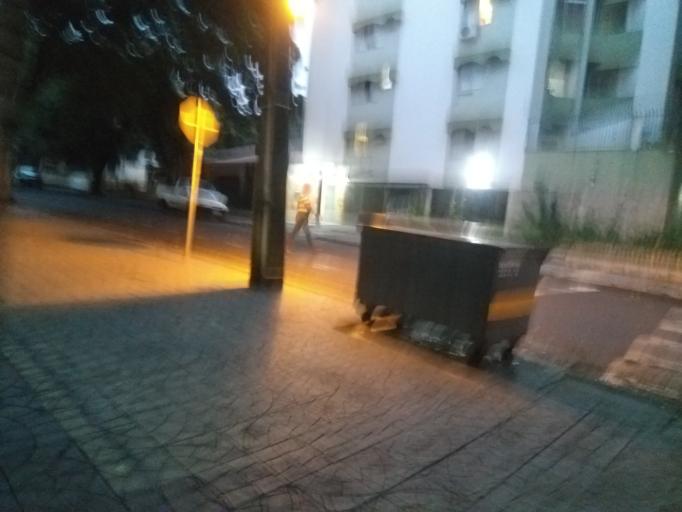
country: BR
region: Parana
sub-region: Maringa
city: Maringa
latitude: -23.4153
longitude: -51.9319
